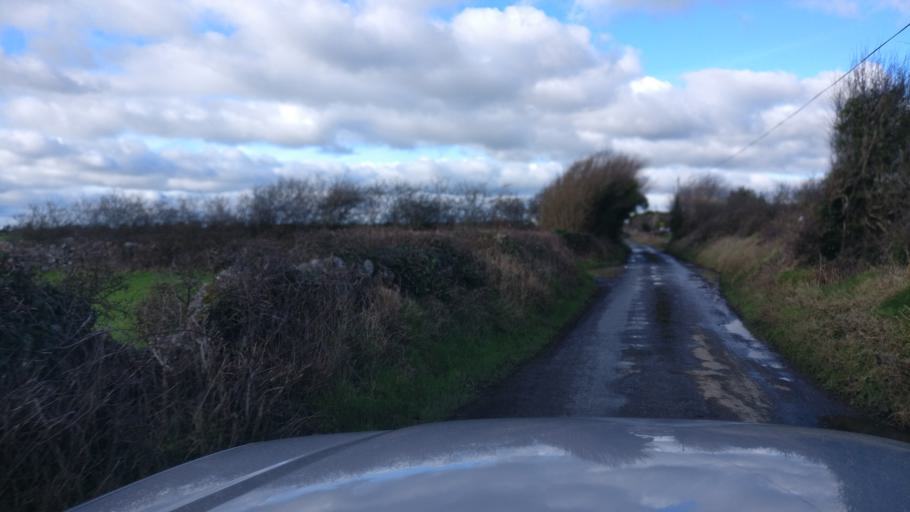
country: IE
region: Connaught
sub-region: County Galway
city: Athenry
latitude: 53.2312
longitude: -8.8007
